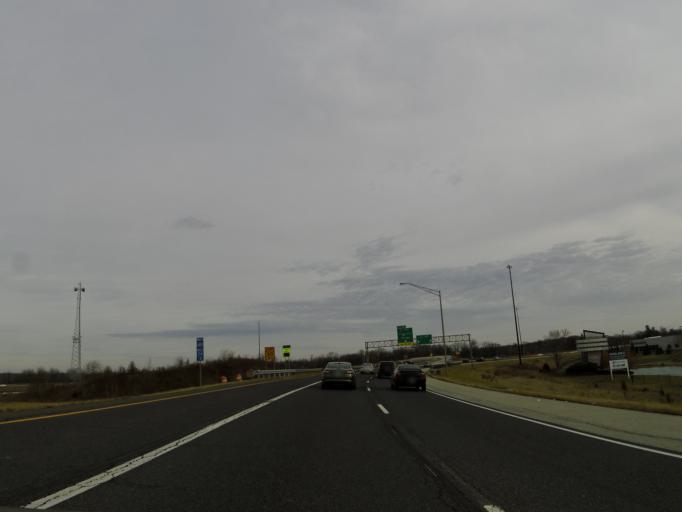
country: US
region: Indiana
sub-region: Boone County
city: Zionsville
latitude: 39.9268
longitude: -86.2673
